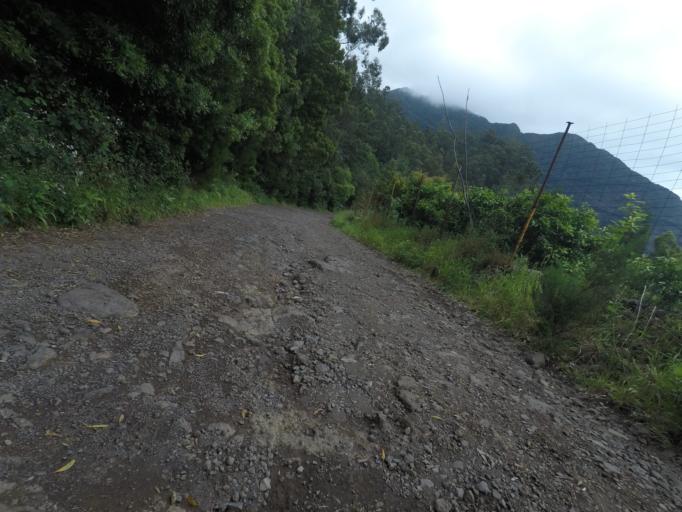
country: PT
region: Madeira
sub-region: Sao Vicente
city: Sao Vicente
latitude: 32.7787
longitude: -17.0487
